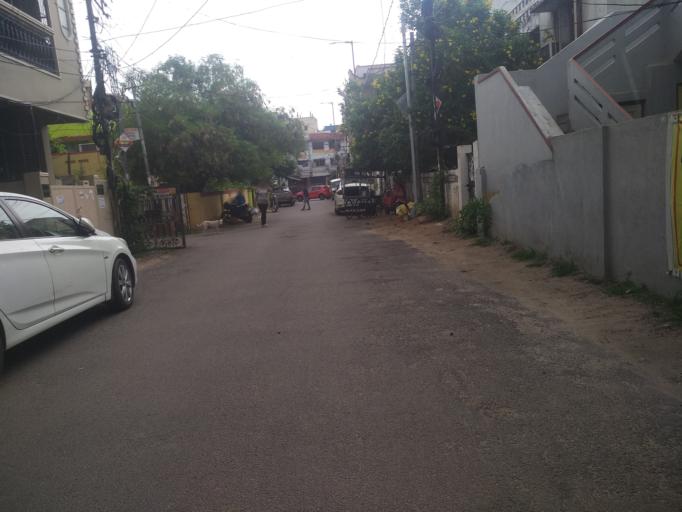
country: IN
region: Telangana
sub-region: Hyderabad
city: Hyderabad
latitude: 17.4342
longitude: 78.4496
